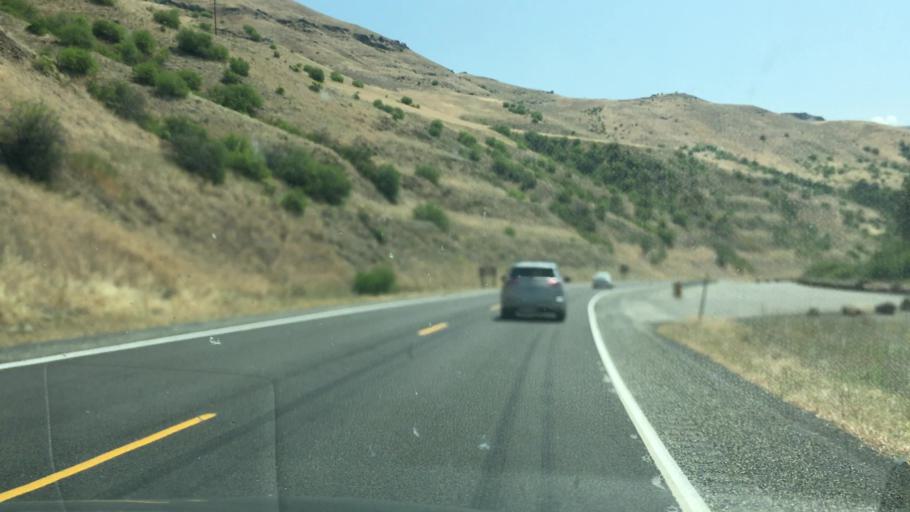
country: US
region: Idaho
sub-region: Idaho County
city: Grangeville
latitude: 45.7345
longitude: -116.3047
